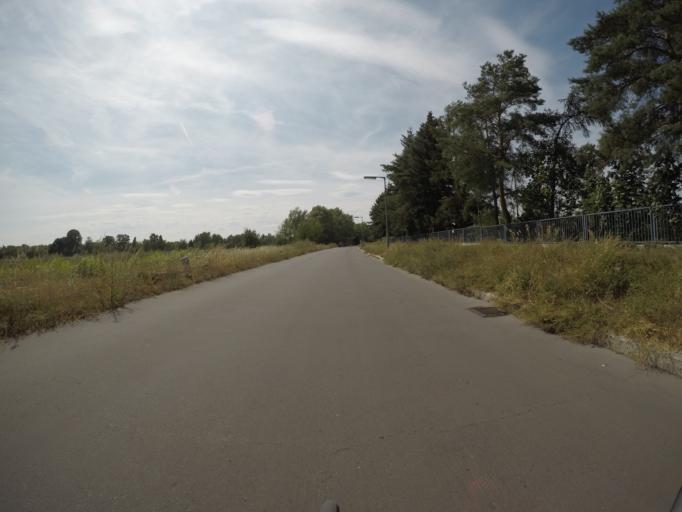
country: DE
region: Berlin
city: Marienfelde
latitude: 52.3956
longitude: 13.3738
